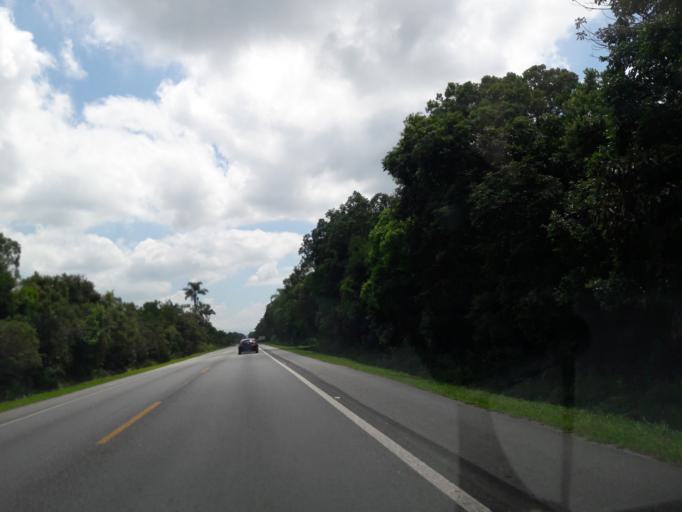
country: BR
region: Parana
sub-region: Pontal Do Parana
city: Pontal do Parana
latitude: -25.6204
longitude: -48.5457
